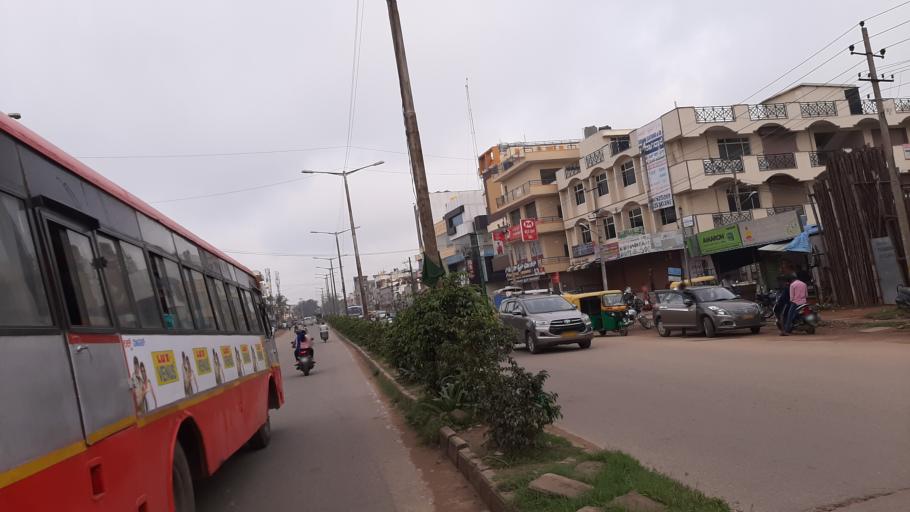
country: IN
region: Karnataka
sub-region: Bangalore Urban
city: Bangalore
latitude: 12.9869
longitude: 77.4763
